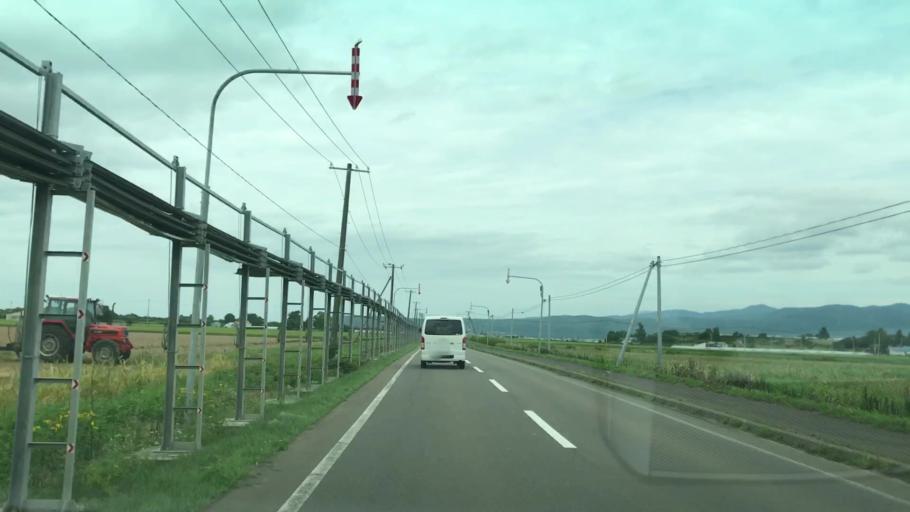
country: JP
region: Hokkaido
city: Iwanai
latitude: 42.9945
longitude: 140.5989
